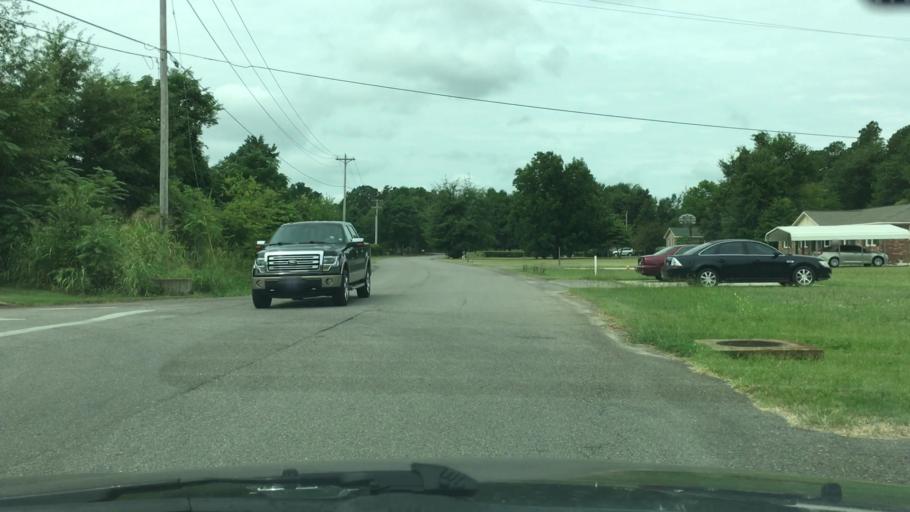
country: US
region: South Carolina
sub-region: Aiken County
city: Aiken
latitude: 33.5034
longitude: -81.7091
